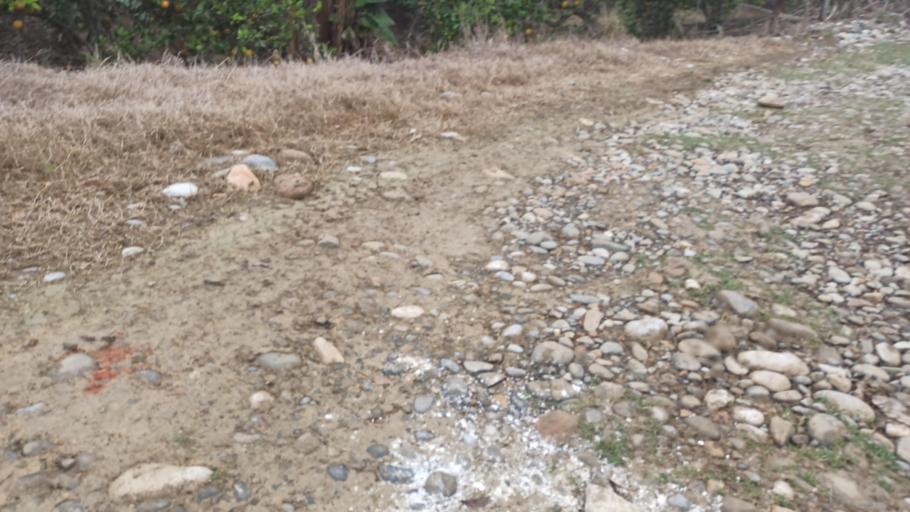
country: MX
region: Veracruz
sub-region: Papantla
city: El Chote
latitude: 20.3832
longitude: -97.3579
